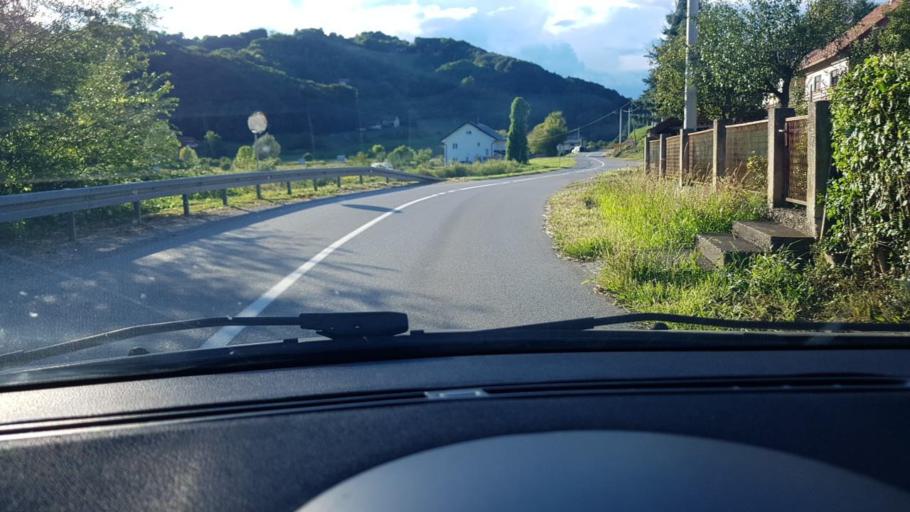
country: HR
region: Krapinsko-Zagorska
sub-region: Grad Krapina
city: Krapina
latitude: 46.0918
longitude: 15.8266
